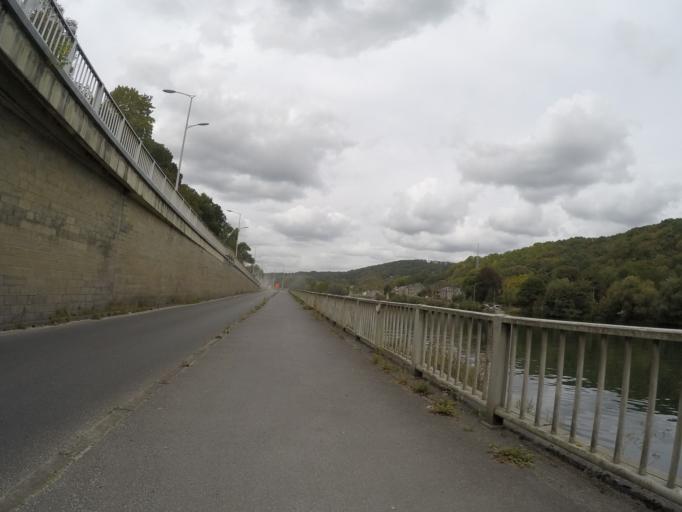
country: BE
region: Wallonia
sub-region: Province de Namur
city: Anhee
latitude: 50.3162
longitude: 4.8765
